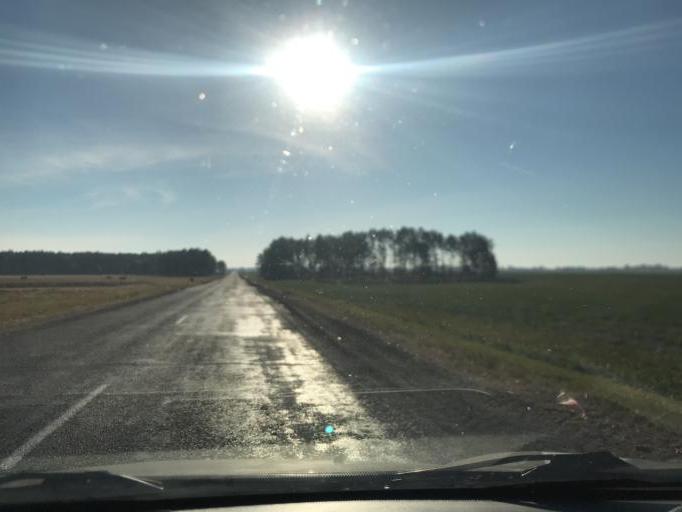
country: BY
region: Gomel
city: Khoyniki
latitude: 51.8159
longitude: 30.0921
